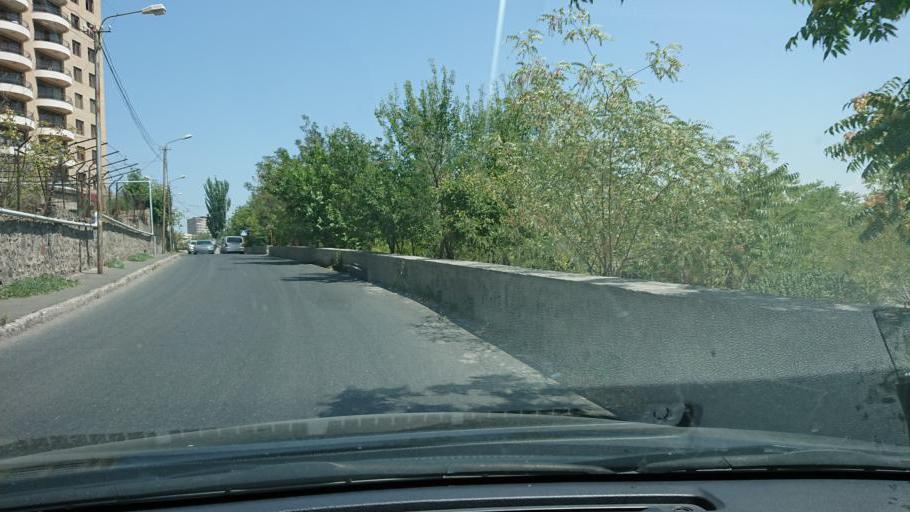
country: AM
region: Yerevan
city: Yerevan
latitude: 40.1938
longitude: 44.5033
